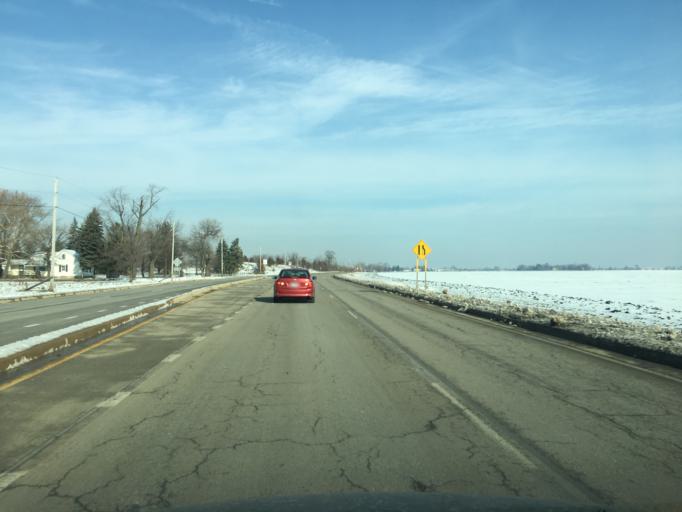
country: US
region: Illinois
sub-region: Will County
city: Plainfield
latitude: 41.6675
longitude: -88.1760
